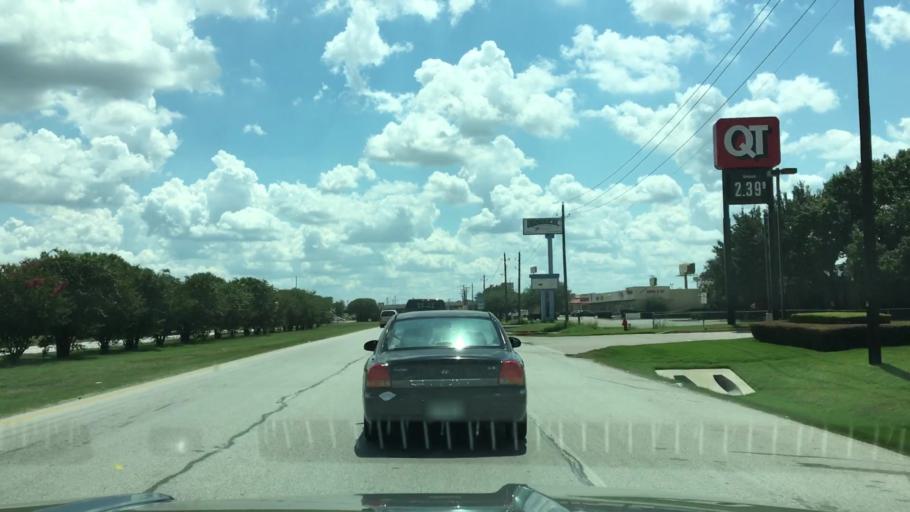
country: US
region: Texas
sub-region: Tarrant County
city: Blue Mound
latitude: 32.8475
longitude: -97.3431
